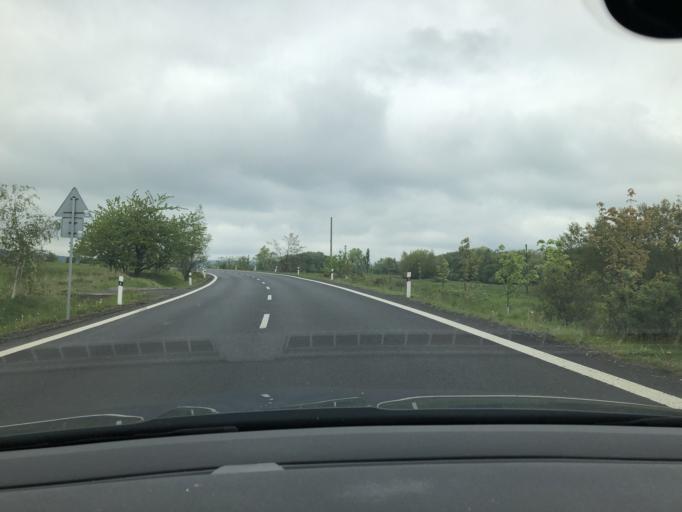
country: CZ
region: Ustecky
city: Libouchec
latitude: 50.7243
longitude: 14.0116
